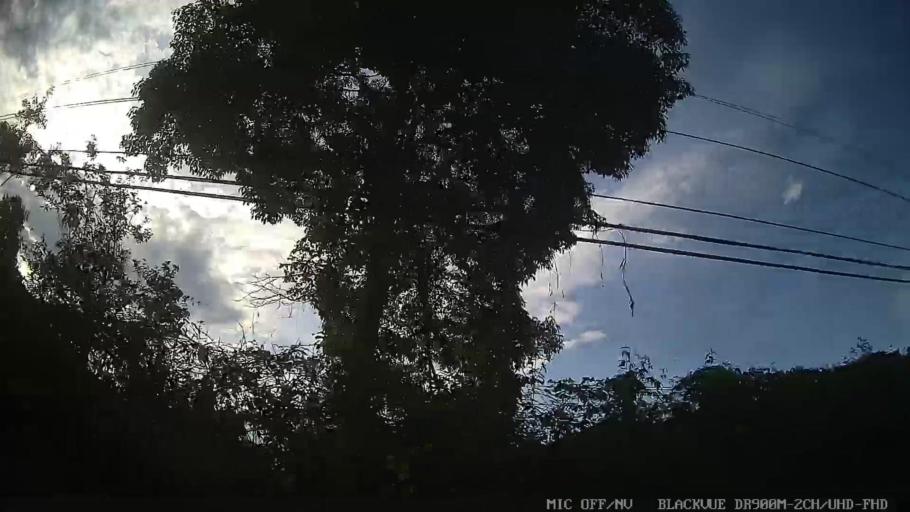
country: BR
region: Sao Paulo
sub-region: Serra Negra
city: Serra Negra
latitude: -22.7039
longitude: -46.6587
